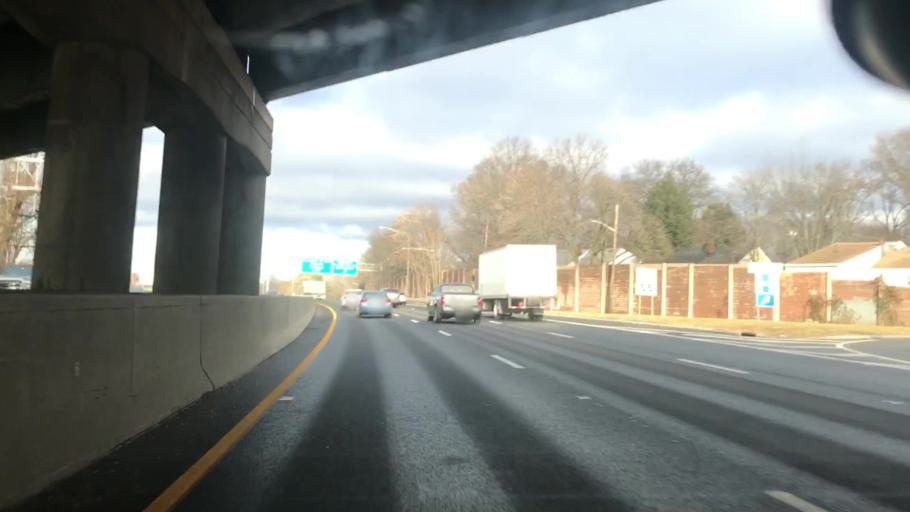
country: US
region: New Jersey
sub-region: Bergen County
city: Ho-Ho-Kus
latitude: 40.9804
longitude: -74.0845
